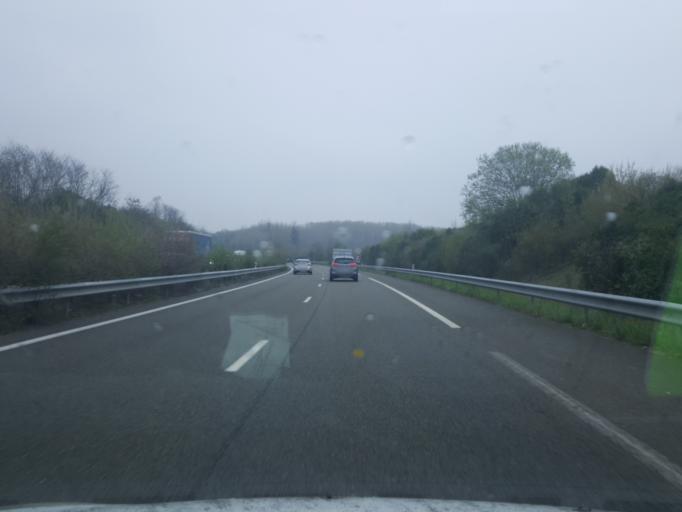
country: FR
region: Ile-de-France
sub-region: Departement des Yvelines
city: Houdan
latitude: 48.7839
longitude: 1.6199
